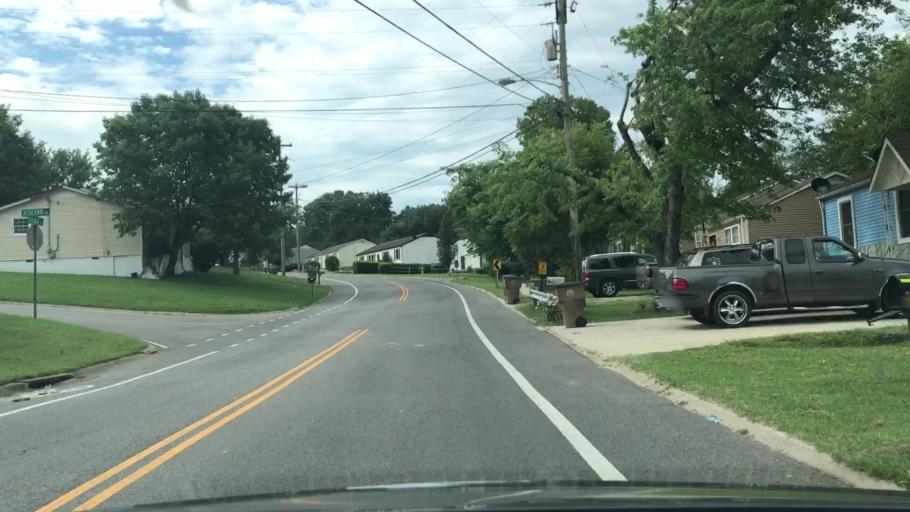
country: US
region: Tennessee
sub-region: Williamson County
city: Brentwood Estates
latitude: 36.0502
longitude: -86.7030
